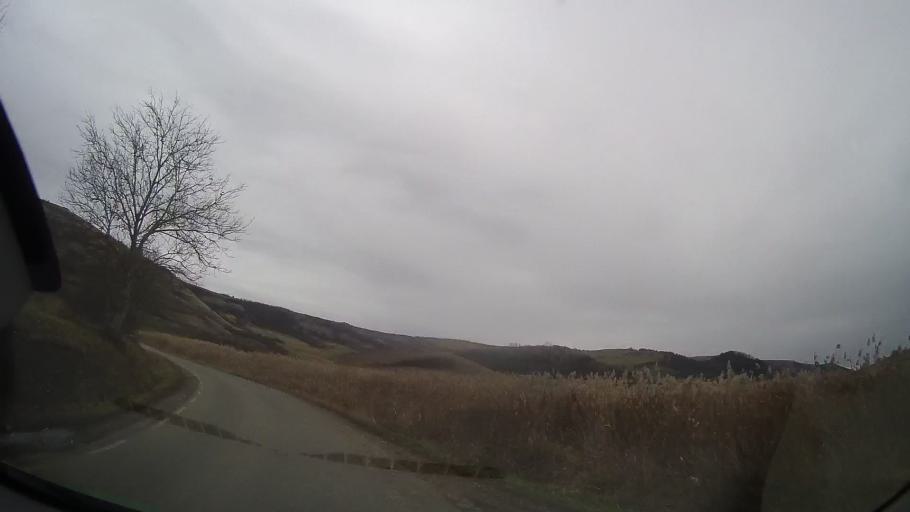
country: RO
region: Mures
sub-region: Comuna Bala
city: Bala
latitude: 46.7155
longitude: 24.5510
